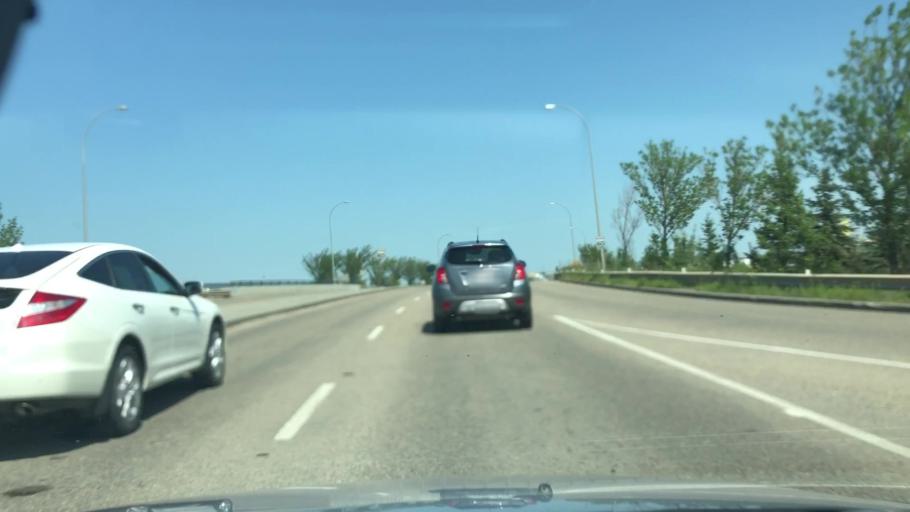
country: CA
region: Alberta
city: St. Albert
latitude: 53.5800
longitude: -113.5910
